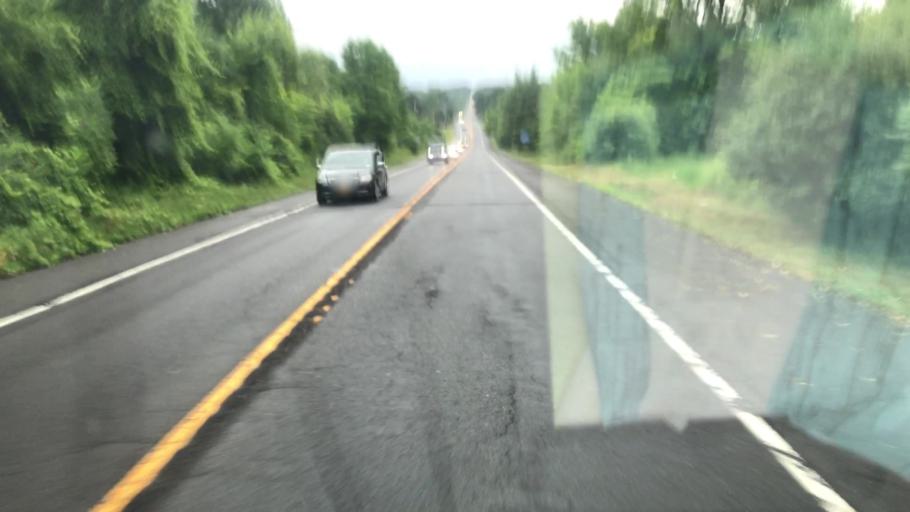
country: US
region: New York
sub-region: Onondaga County
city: Fayetteville
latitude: 43.0248
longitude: -76.0372
